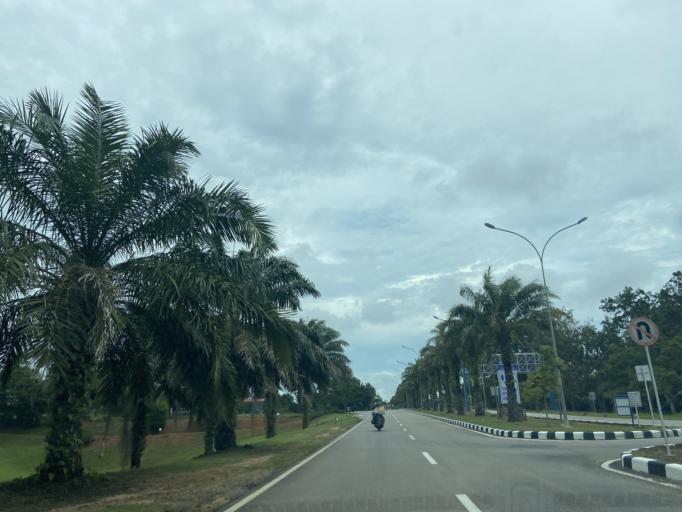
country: SG
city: Singapore
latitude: 1.1257
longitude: 104.1147
